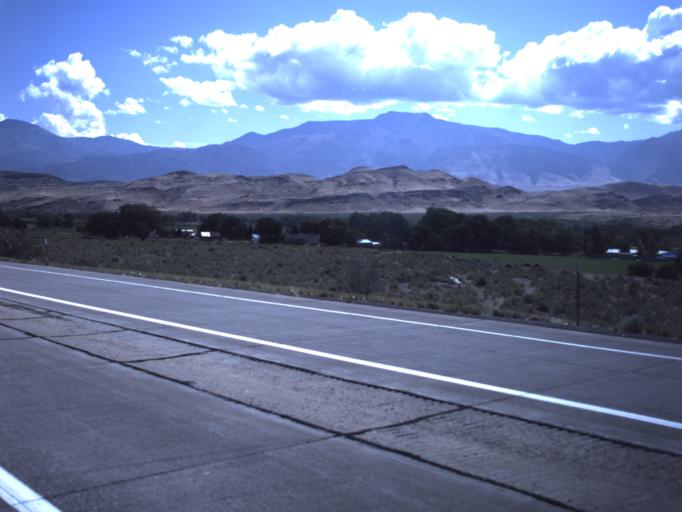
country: US
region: Utah
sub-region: Sevier County
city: Monroe
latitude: 38.6004
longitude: -112.2512
